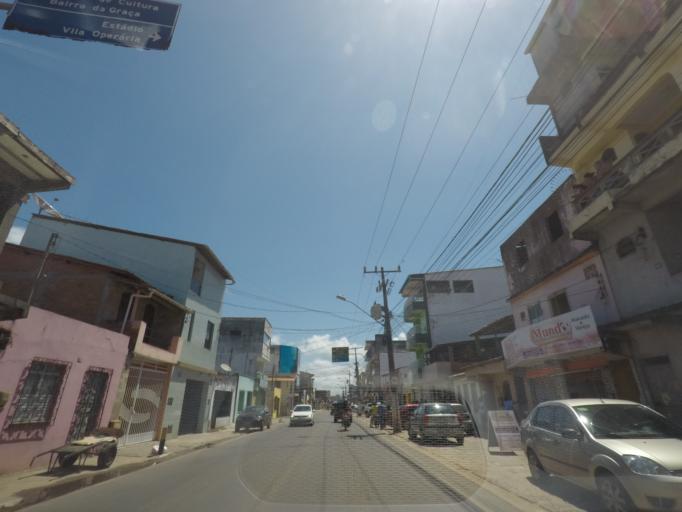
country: BR
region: Bahia
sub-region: Valenca
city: Valenca
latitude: -13.3641
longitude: -39.0690
